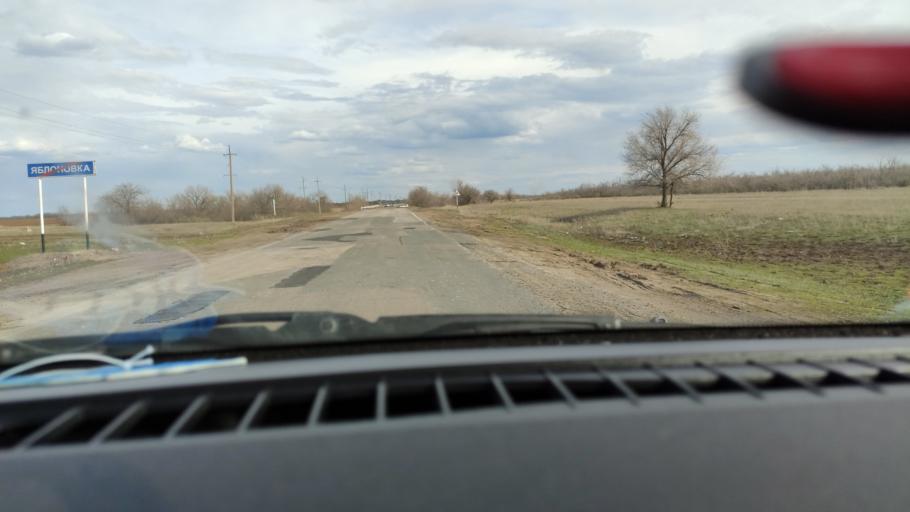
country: RU
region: Saratov
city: Rovnoye
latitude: 51.0562
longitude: 46.0310
